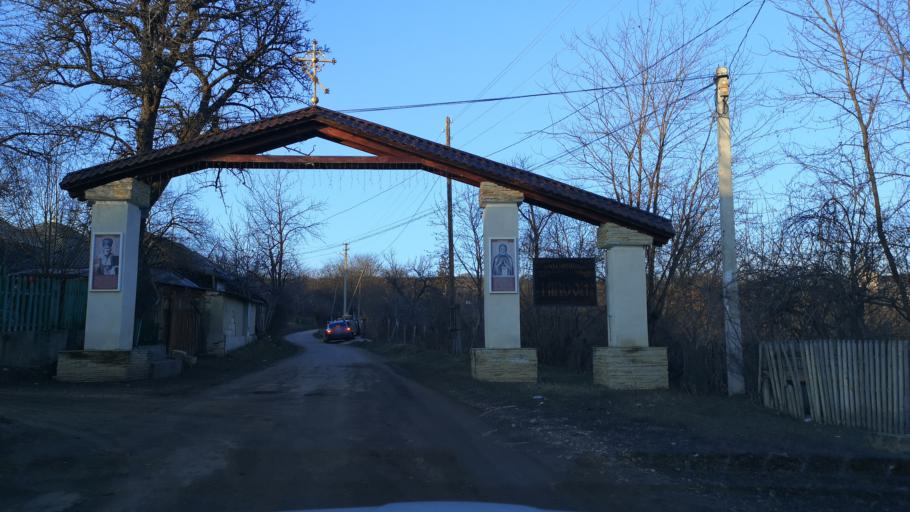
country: MD
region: Orhei
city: Orhei
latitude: 47.3662
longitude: 28.6904
